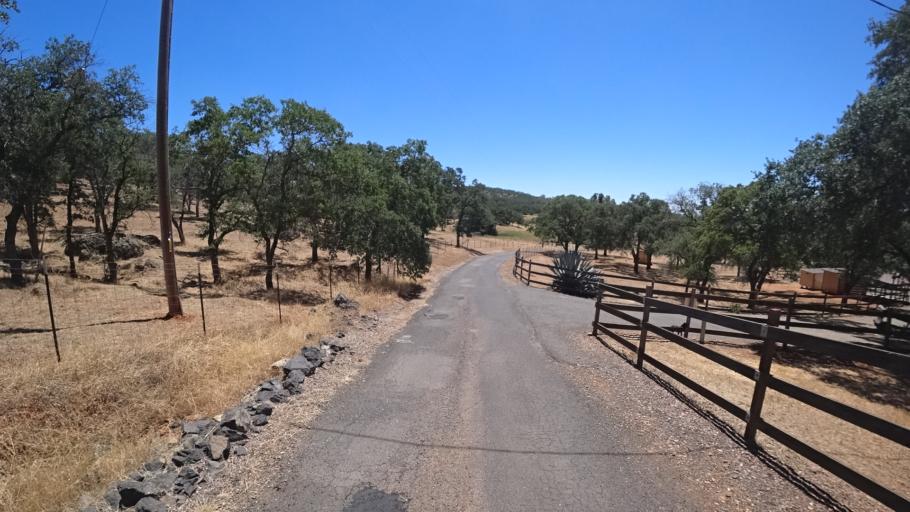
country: US
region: California
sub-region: Calaveras County
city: Copperopolis
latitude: 37.9879
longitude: -120.6656
